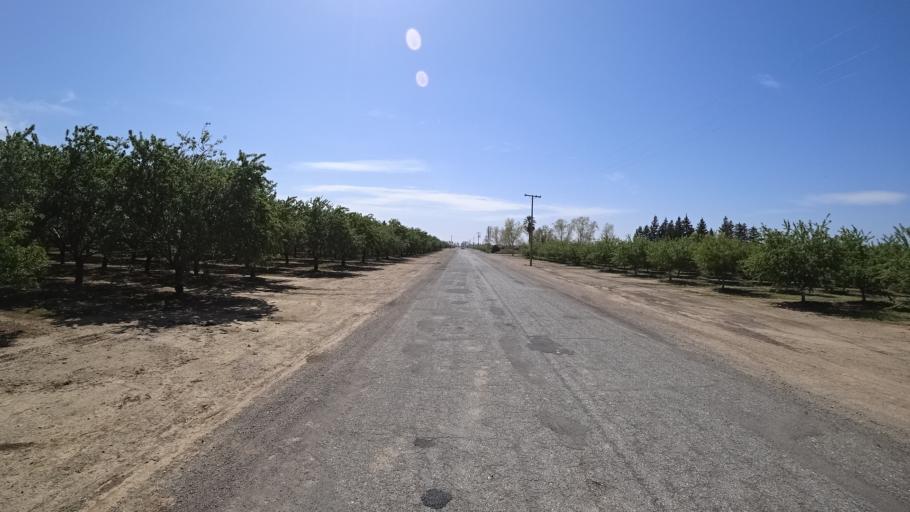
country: US
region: California
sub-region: Glenn County
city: Hamilton City
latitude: 39.6518
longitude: -122.0742
